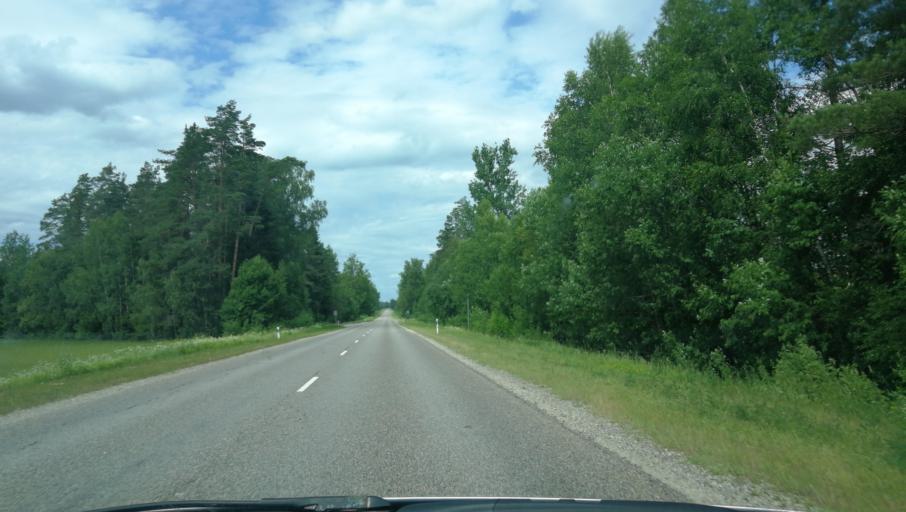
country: LV
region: Naukseni
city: Naukseni
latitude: 57.8126
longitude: 25.4053
